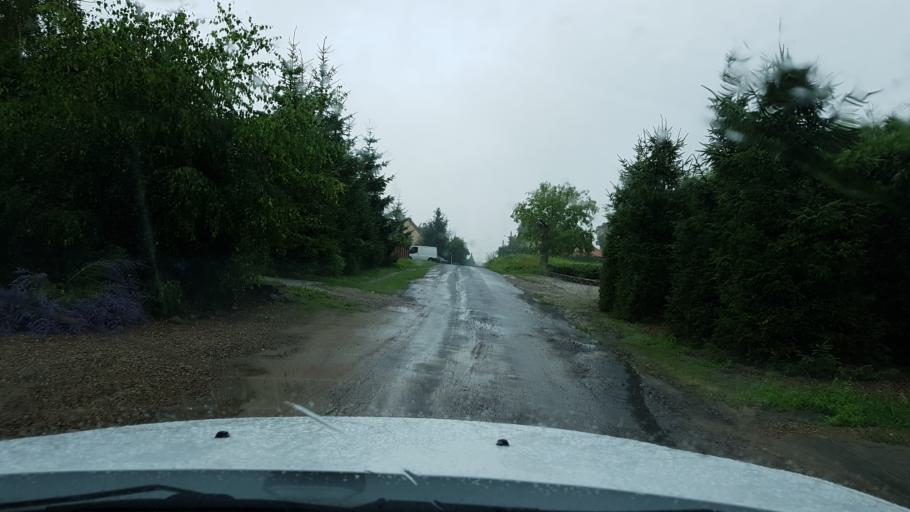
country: PL
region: West Pomeranian Voivodeship
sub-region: Powiat gryfinski
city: Chojna
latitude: 52.9528
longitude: 14.4260
